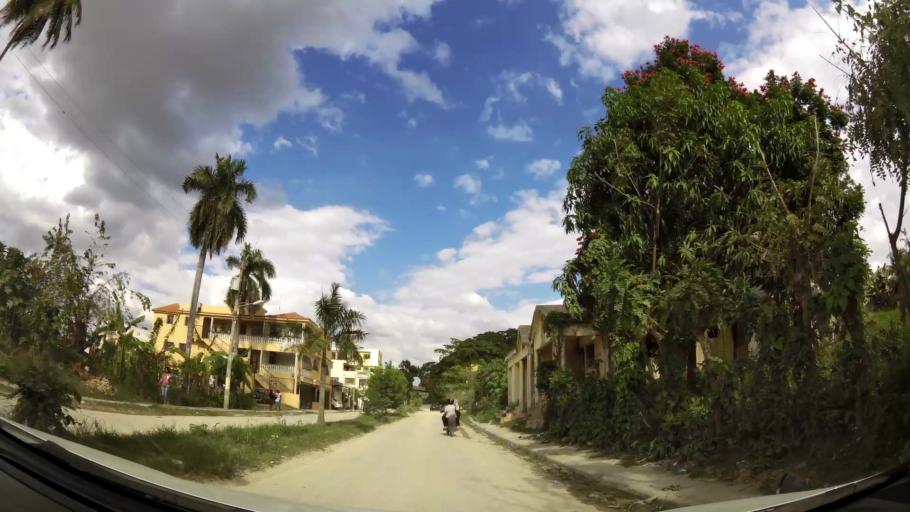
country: DO
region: Nacional
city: Ensanche Luperon
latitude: 18.5553
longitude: -69.9000
